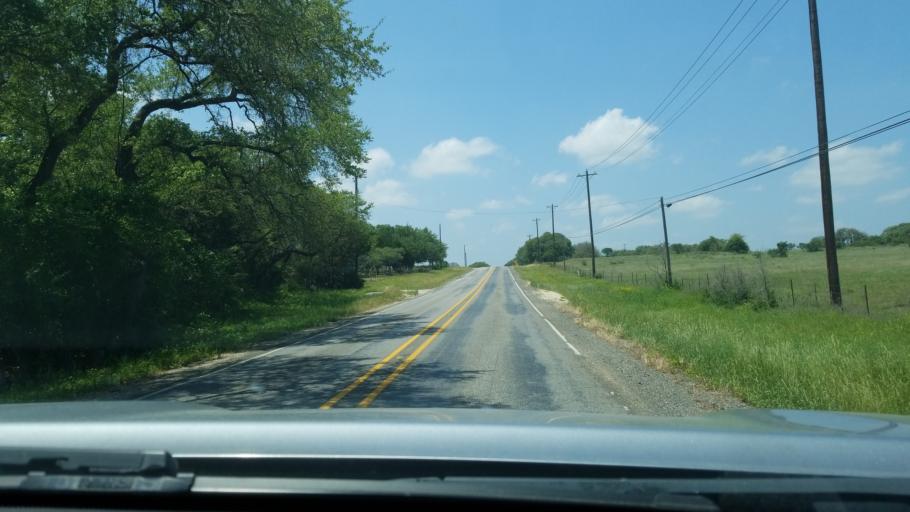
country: US
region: Texas
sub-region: Hays County
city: Woodcreek
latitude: 30.0386
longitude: -98.1867
